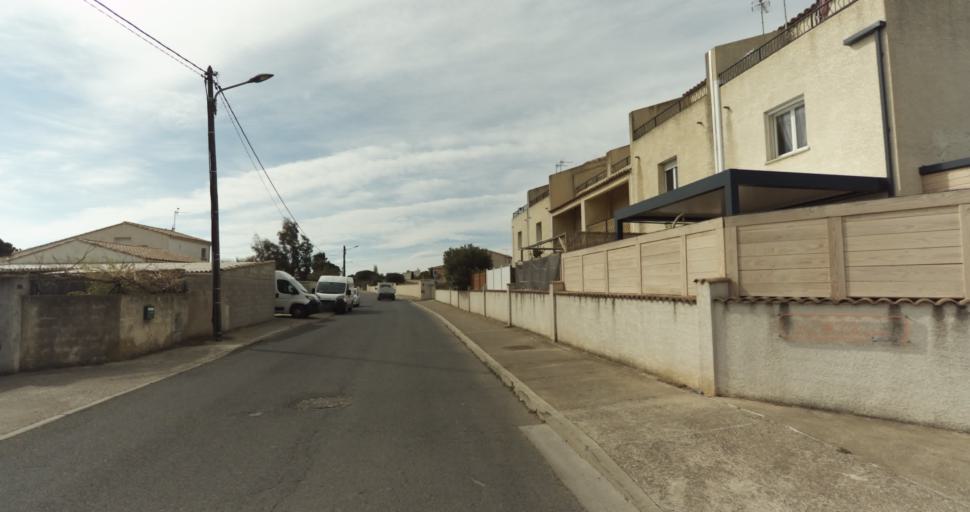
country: FR
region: Languedoc-Roussillon
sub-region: Departement de l'Herault
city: Marseillan
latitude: 43.3350
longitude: 3.5287
